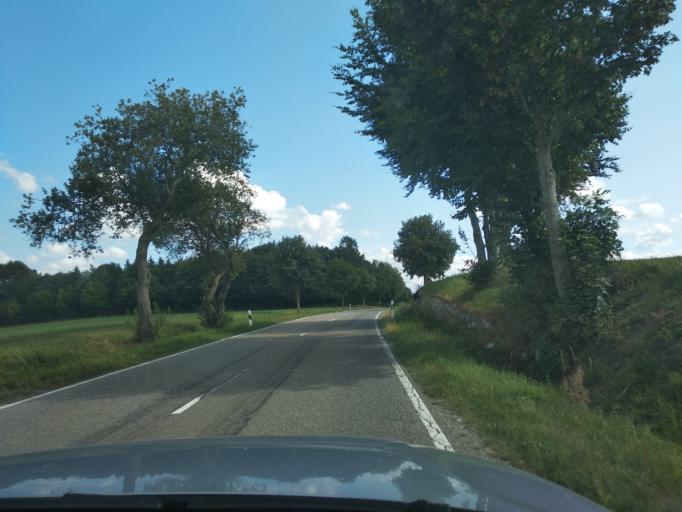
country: DE
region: Baden-Wuerttemberg
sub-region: Tuebingen Region
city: Leutkirch im Allgau
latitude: 47.8833
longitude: 9.9842
